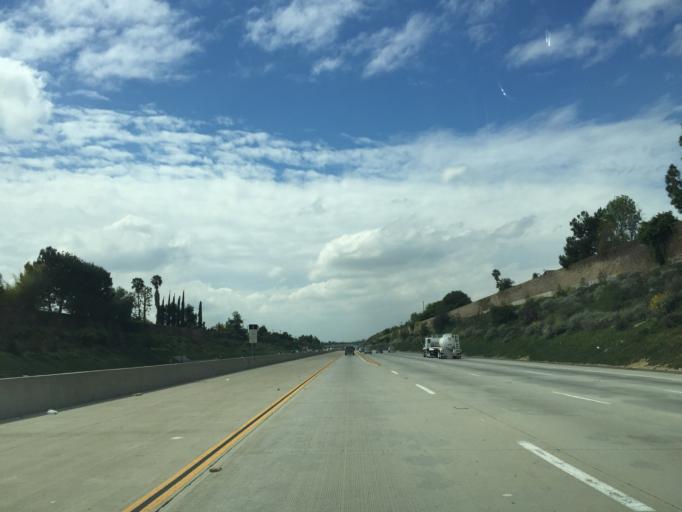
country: US
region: California
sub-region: Los Angeles County
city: Claremont
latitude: 34.1201
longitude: -117.7104
